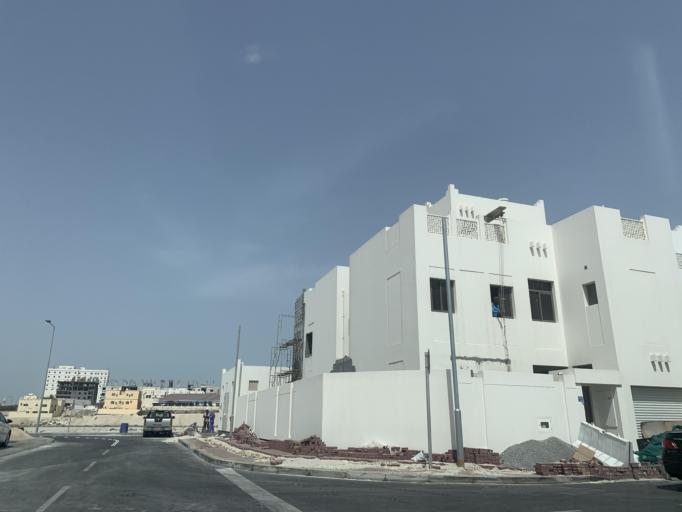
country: BH
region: Northern
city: Ar Rifa'
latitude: 26.1496
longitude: 50.5647
